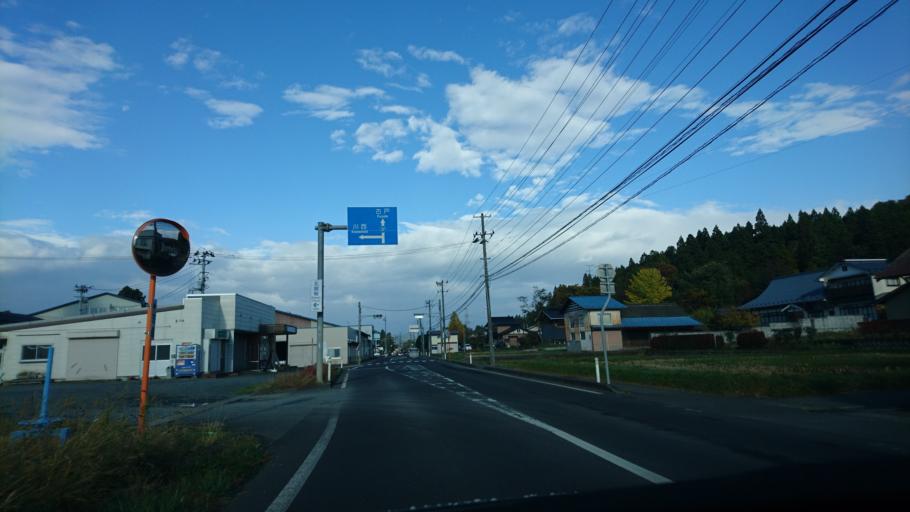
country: JP
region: Iwate
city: Ichinoseki
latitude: 39.0196
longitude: 141.0940
